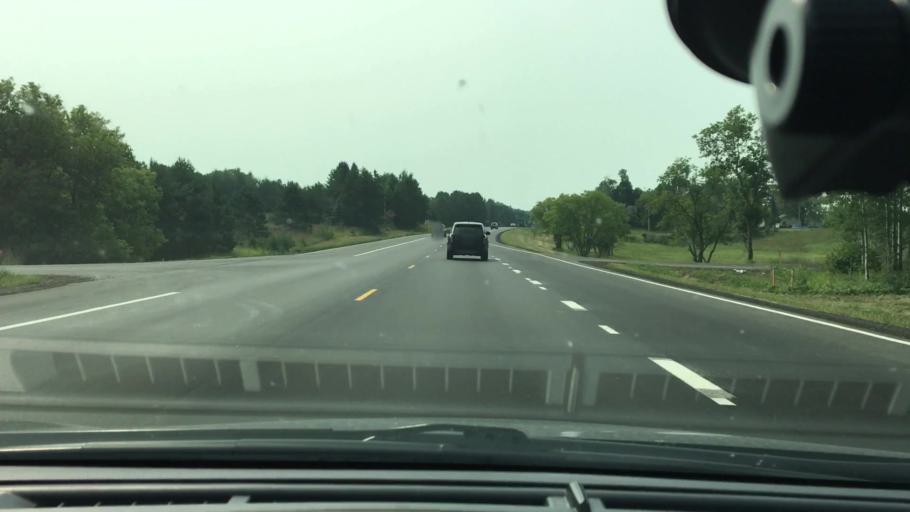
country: US
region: Minnesota
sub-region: Crow Wing County
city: Brainerd
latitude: 46.4062
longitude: -94.1760
